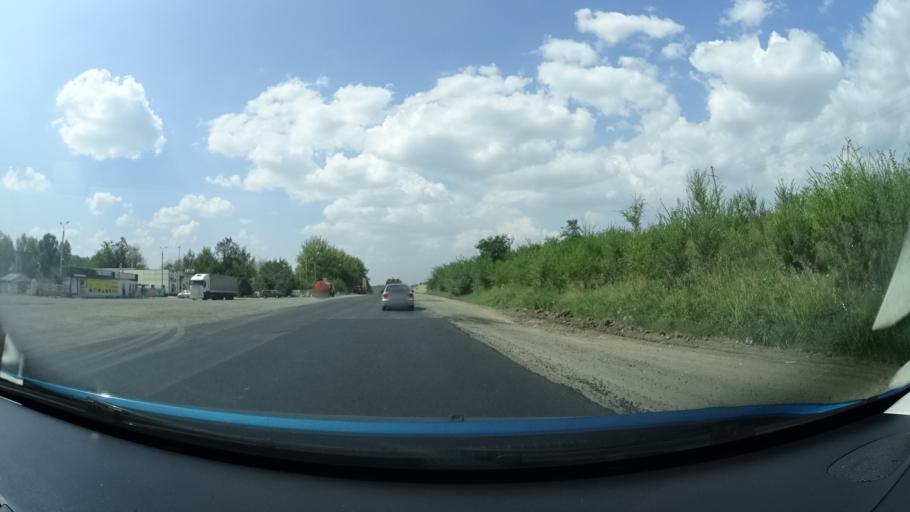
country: RU
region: Bashkortostan
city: Kandry
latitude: 54.5140
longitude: 54.0265
